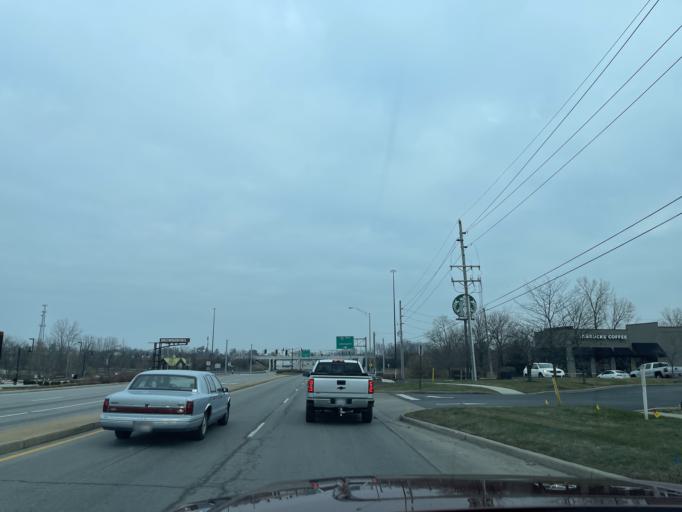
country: US
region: Indiana
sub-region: Hendricks County
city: Brownsburg
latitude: 39.8575
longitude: -86.3924
